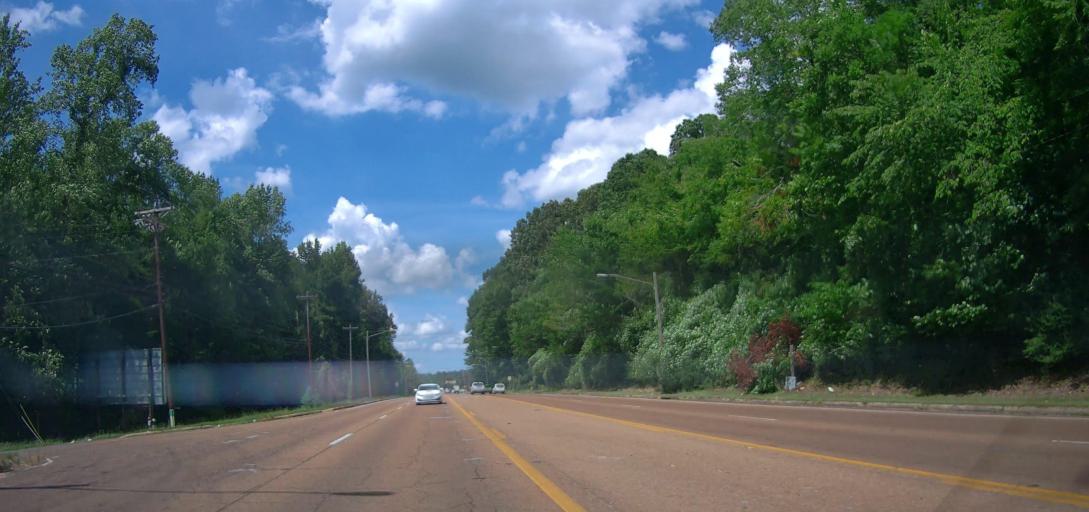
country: US
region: Mississippi
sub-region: Lowndes County
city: Columbus
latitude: 33.5424
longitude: -88.4370
